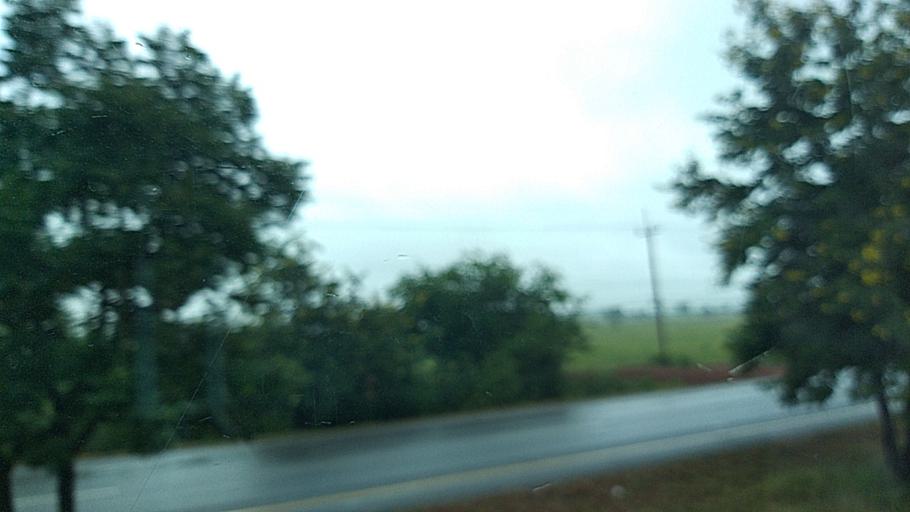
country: TH
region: Nakhon Ratchasima
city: Non Sung
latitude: 15.2127
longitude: 102.3577
